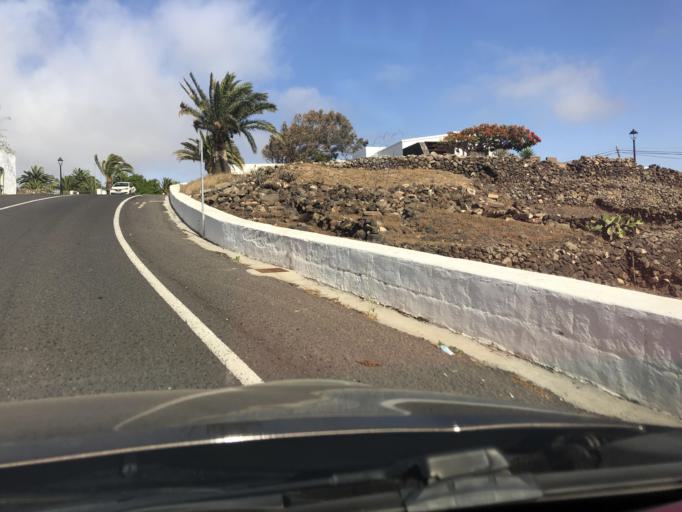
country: ES
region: Canary Islands
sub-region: Provincia de Las Palmas
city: Yaiza
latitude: 28.9524
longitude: -13.7620
